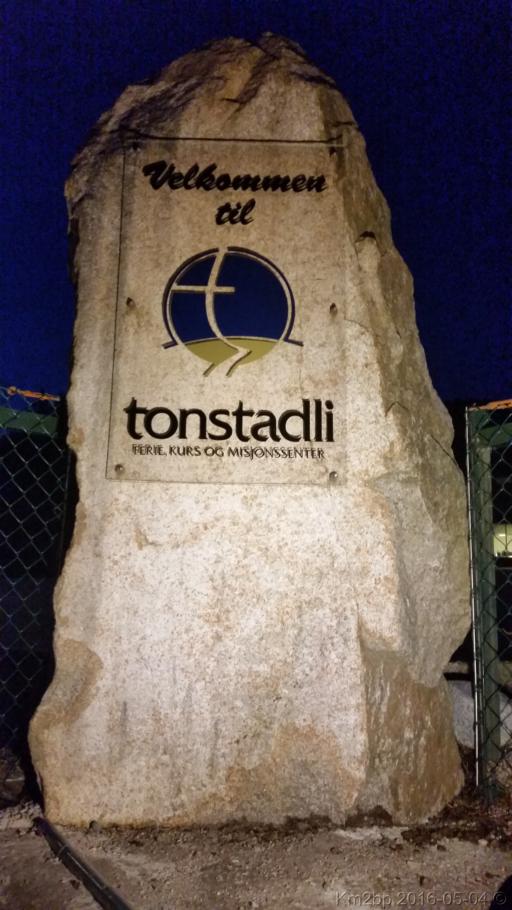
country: NO
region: Vest-Agder
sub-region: Sirdal
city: Tonstad
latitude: 58.6666
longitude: 6.7305
